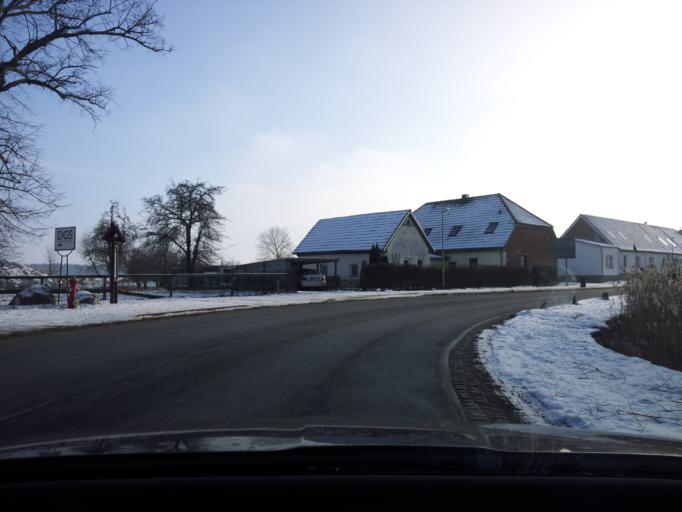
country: DE
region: Mecklenburg-Vorpommern
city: Blowatz
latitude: 53.9620
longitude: 11.4897
